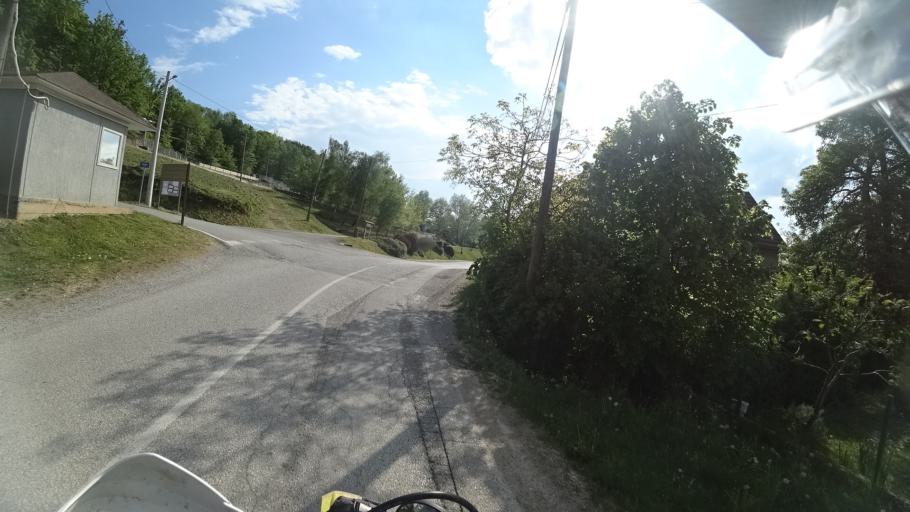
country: HR
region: Zagrebacka
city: Jablanovec
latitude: 45.8961
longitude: 15.8791
